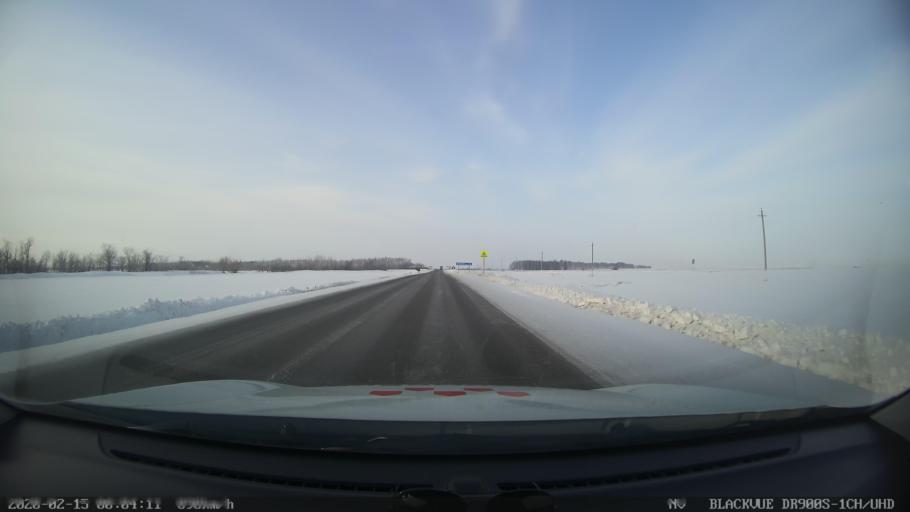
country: RU
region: Tatarstan
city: Kuybyshevskiy Zaton
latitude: 55.3798
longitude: 48.9871
